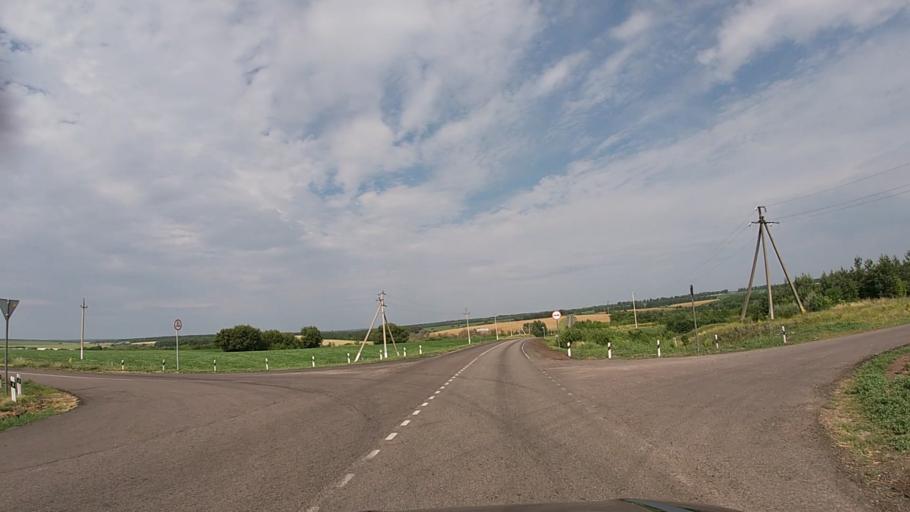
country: RU
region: Belgorod
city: Krasnaya Yaruga
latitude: 50.7985
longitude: 35.5795
